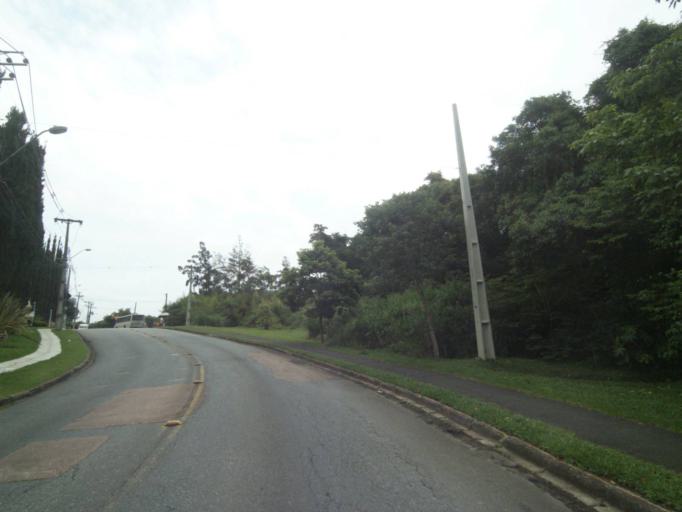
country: BR
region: Parana
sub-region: Curitiba
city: Curitiba
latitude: -25.4074
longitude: -49.3038
